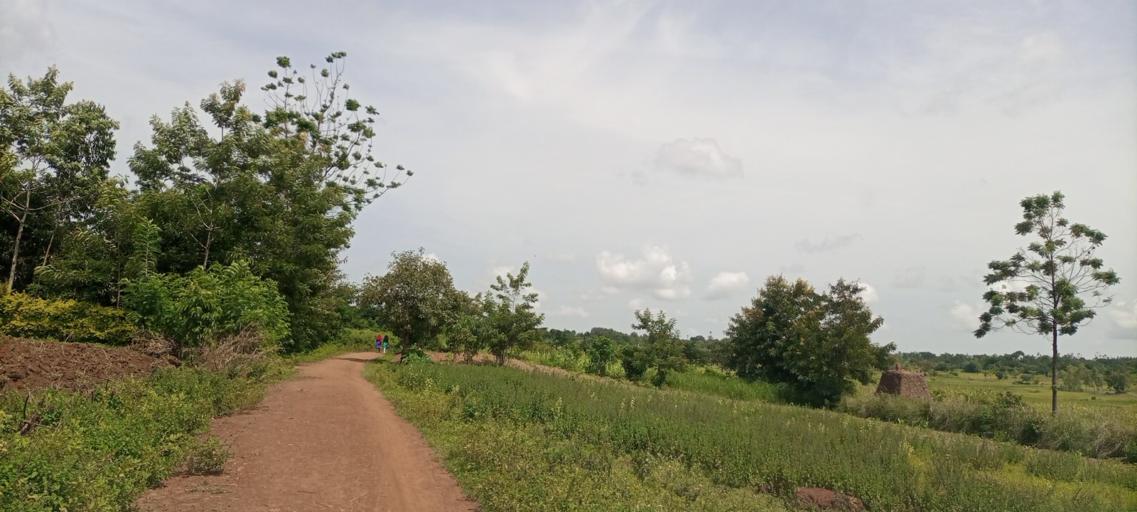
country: UG
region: Eastern Region
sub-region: Budaka District
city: Budaka
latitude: 1.1730
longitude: 33.9521
